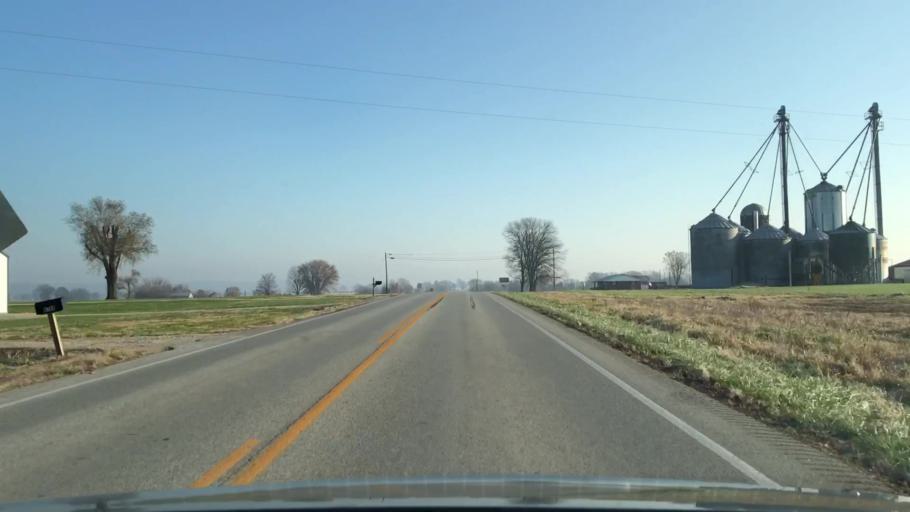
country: US
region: Kentucky
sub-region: Warren County
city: Bowling Green
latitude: 37.0505
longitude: -86.3116
